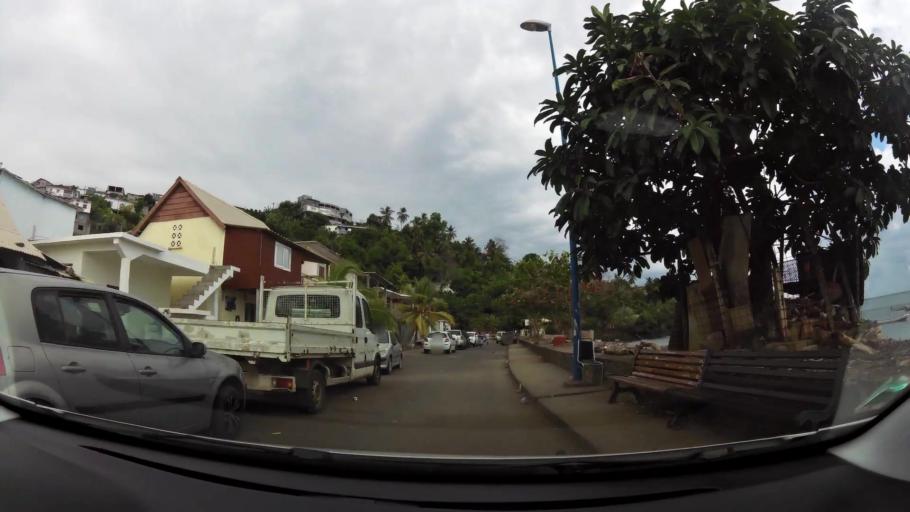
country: YT
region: Sada
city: Sada
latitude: -12.8508
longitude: 45.0971
